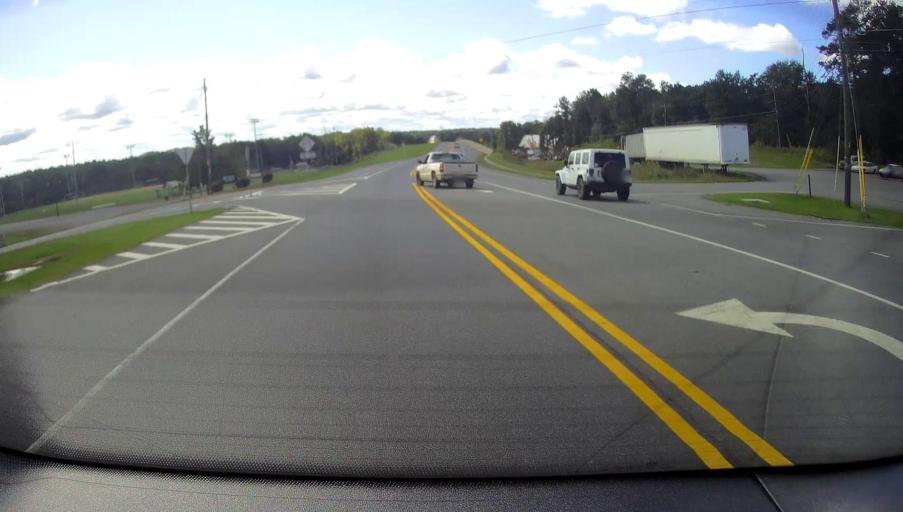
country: US
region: Georgia
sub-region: Bibb County
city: Macon
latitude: 32.8885
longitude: -83.5369
